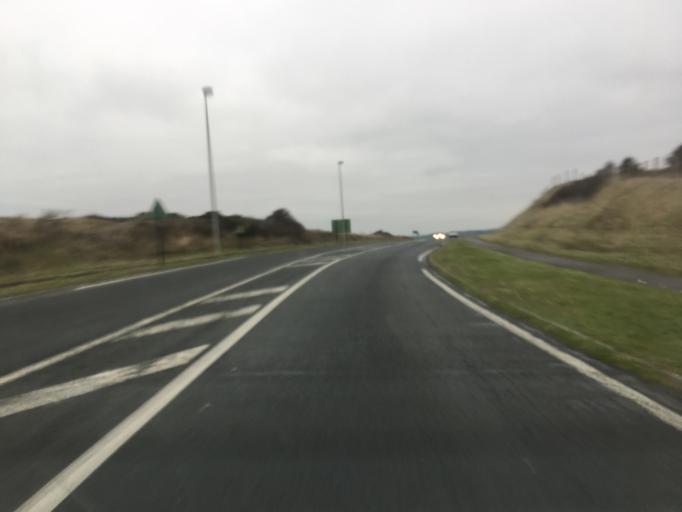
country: FR
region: Nord-Pas-de-Calais
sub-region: Departement du Pas-de-Calais
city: Wimereux
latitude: 50.7490
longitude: 1.5987
